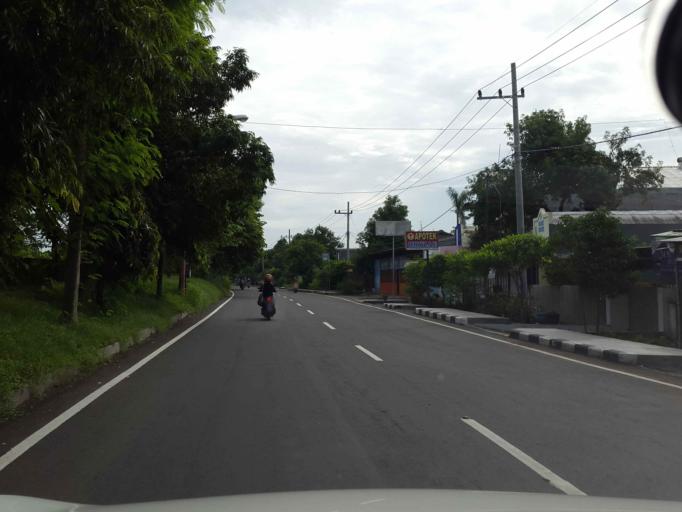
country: ID
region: East Java
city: Mojokerto
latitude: -7.4564
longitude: 112.4411
